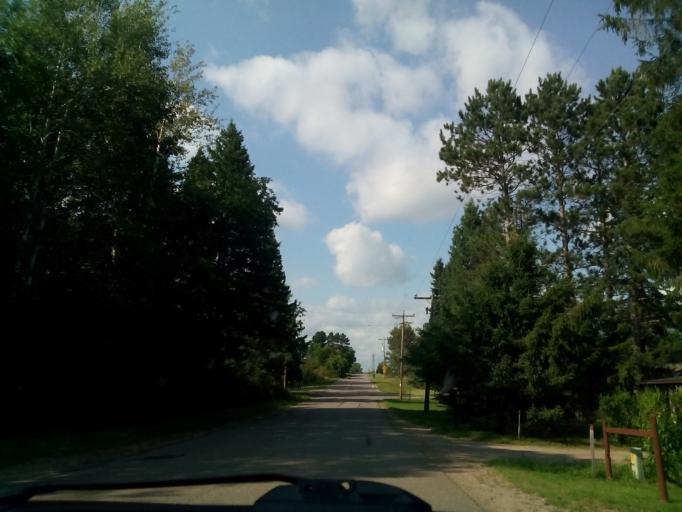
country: US
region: Wisconsin
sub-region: Menominee County
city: Legend Lake
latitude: 45.3048
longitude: -88.5222
